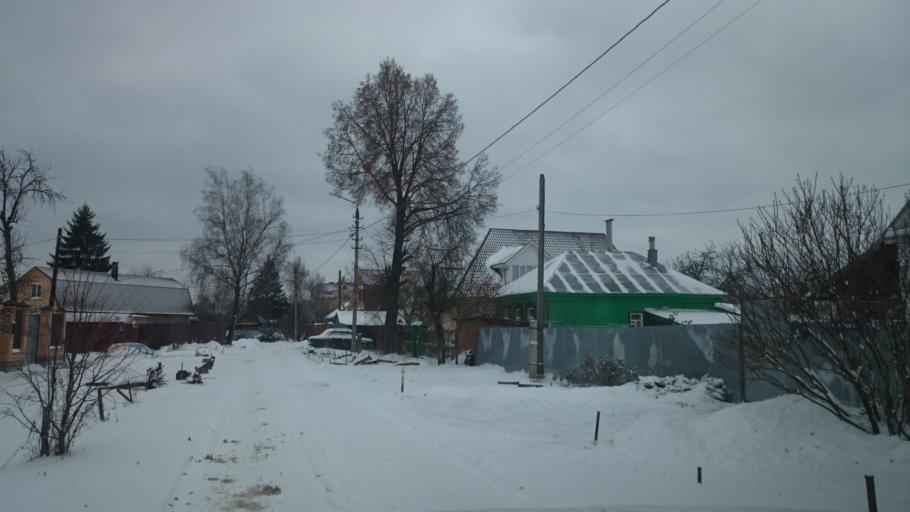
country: RU
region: Tula
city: Tula
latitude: 54.2024
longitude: 37.5635
